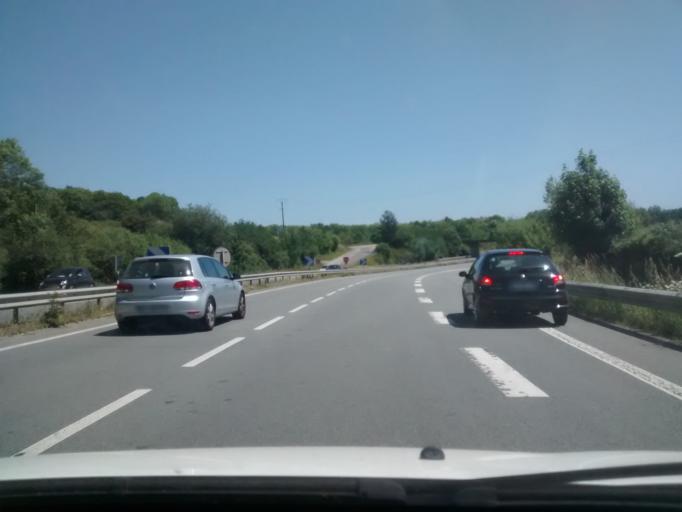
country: FR
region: Brittany
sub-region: Departement d'Ille-et-Vilaine
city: Saint-Pere
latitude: 48.5669
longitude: -1.9271
